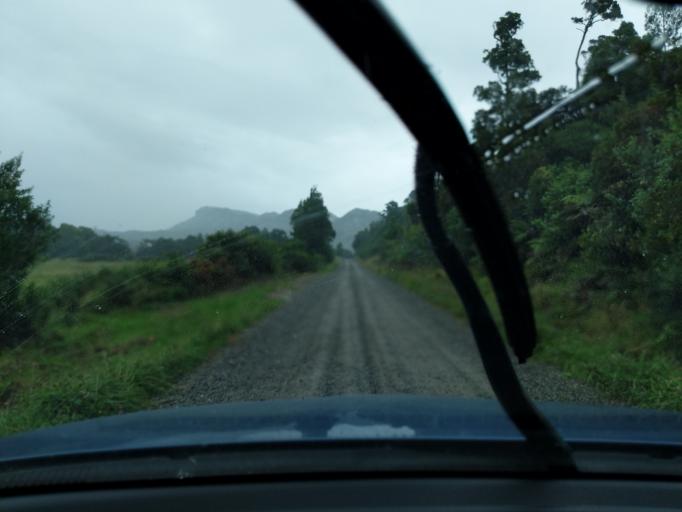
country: NZ
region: Tasman
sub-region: Tasman District
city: Takaka
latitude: -40.6502
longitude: 172.4681
